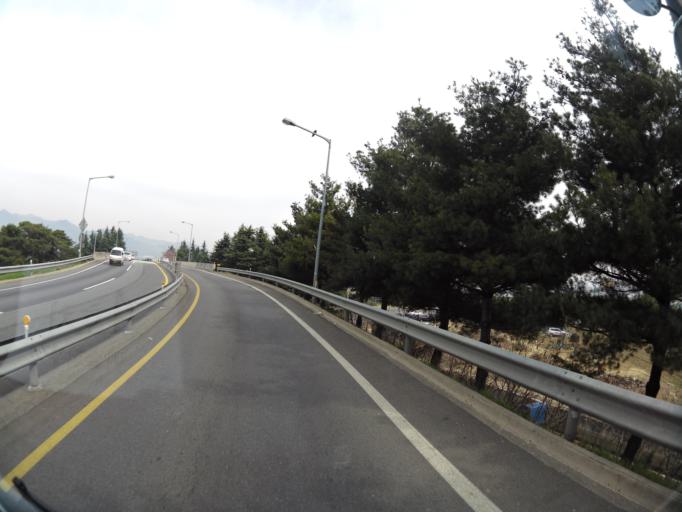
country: KR
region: Gyeongsangbuk-do
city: Hayang
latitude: 35.8736
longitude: 128.7969
